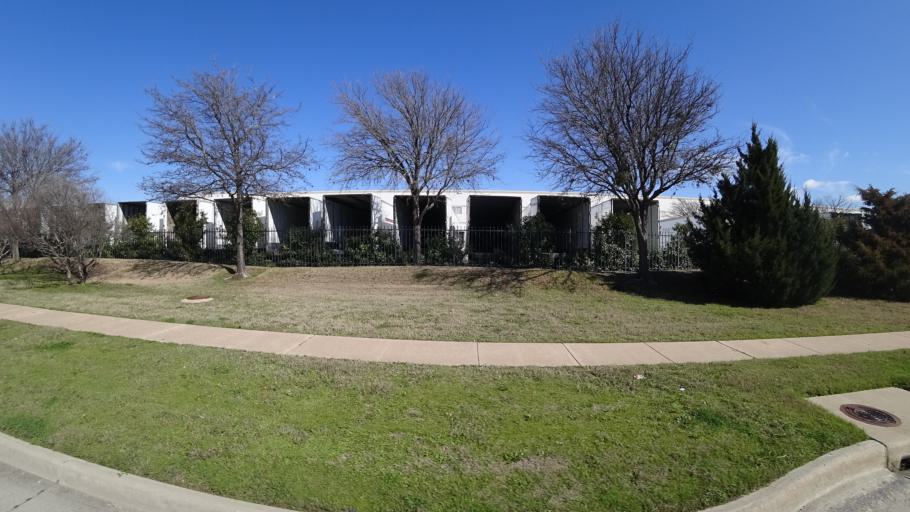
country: US
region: Texas
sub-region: Denton County
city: Lewisville
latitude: 33.0185
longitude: -96.9706
